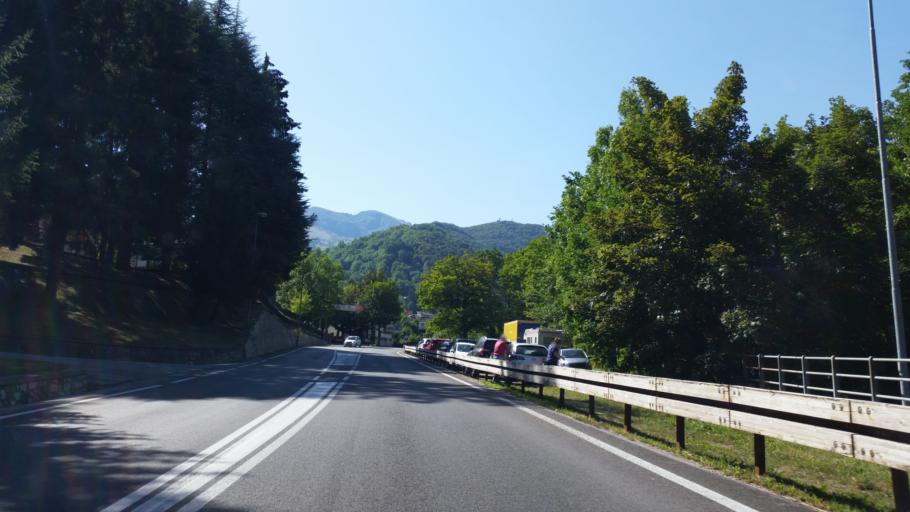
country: IT
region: Piedmont
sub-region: Provincia di Cuneo
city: Limone Piemonte
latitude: 44.2063
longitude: 7.5745
